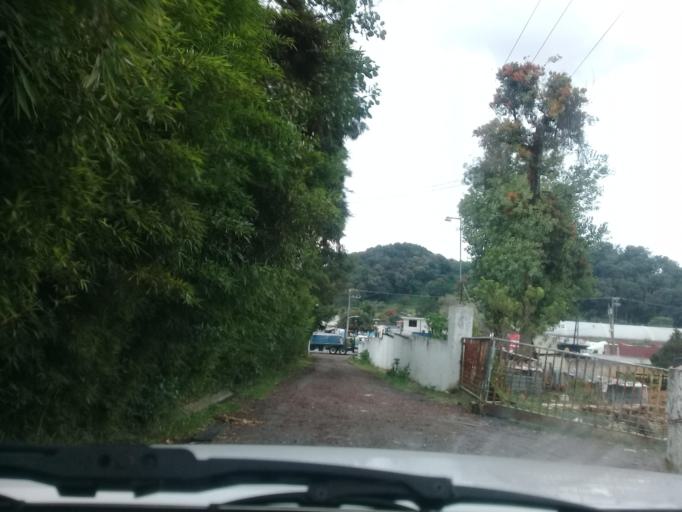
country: MX
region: Veracruz
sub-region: Rafael Lucio
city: Piletas
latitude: 19.5878
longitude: -96.9681
